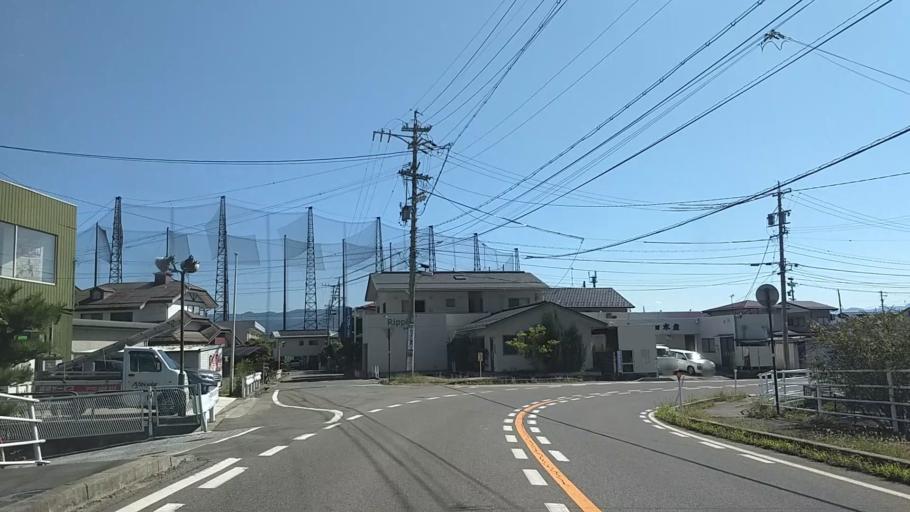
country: JP
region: Nagano
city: Nagano-shi
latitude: 36.6277
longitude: 138.1543
